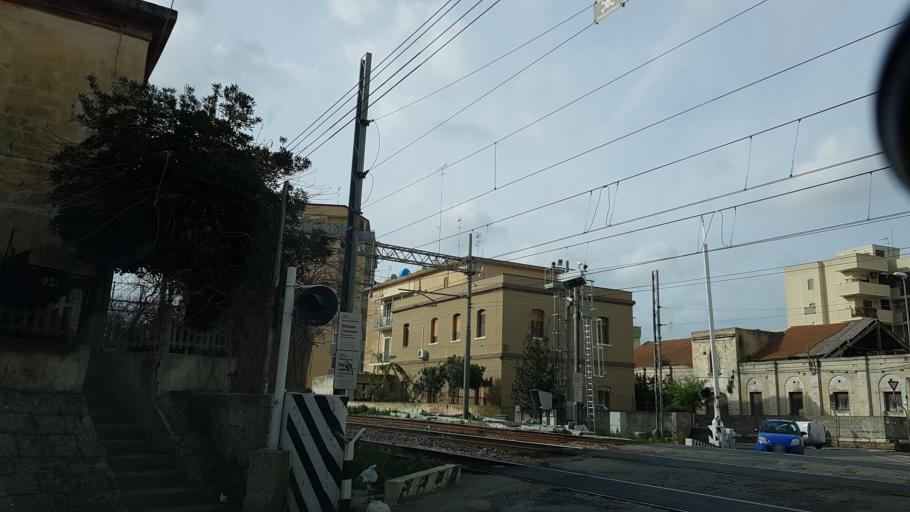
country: IT
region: Apulia
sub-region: Provincia di Brindisi
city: Brindisi
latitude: 40.6373
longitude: 17.9315
